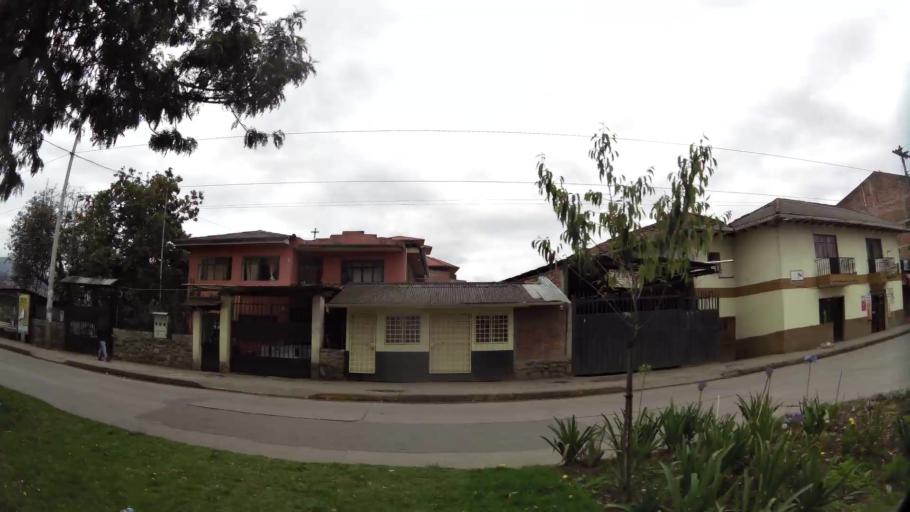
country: EC
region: Azuay
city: Cuenca
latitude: -2.9182
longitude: -79.0349
